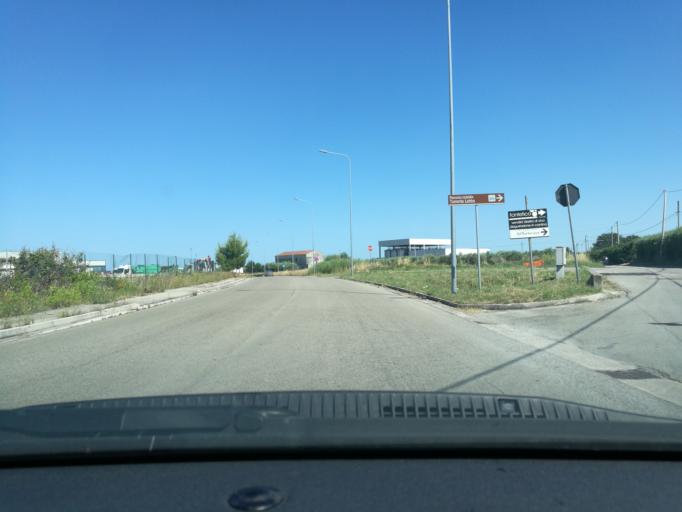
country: IT
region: Abruzzo
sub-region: Provincia di Chieti
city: Vasto
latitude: 42.1651
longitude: 14.6839
